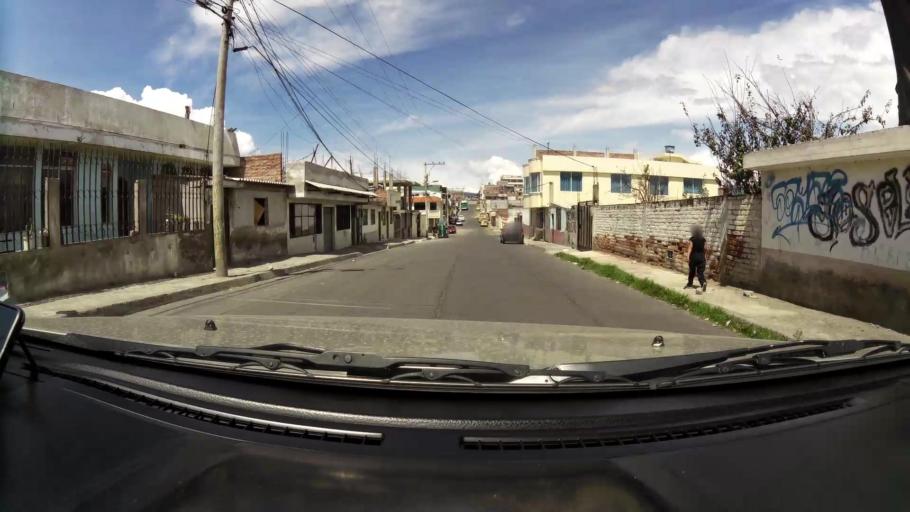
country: EC
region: Chimborazo
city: Riobamba
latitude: -1.6601
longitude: -78.6461
